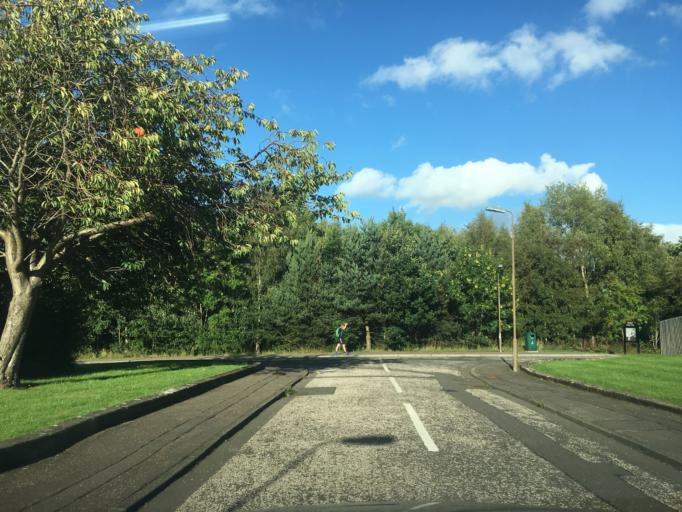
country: GB
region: Scotland
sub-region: Edinburgh
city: Colinton
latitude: 55.9068
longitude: -3.2373
